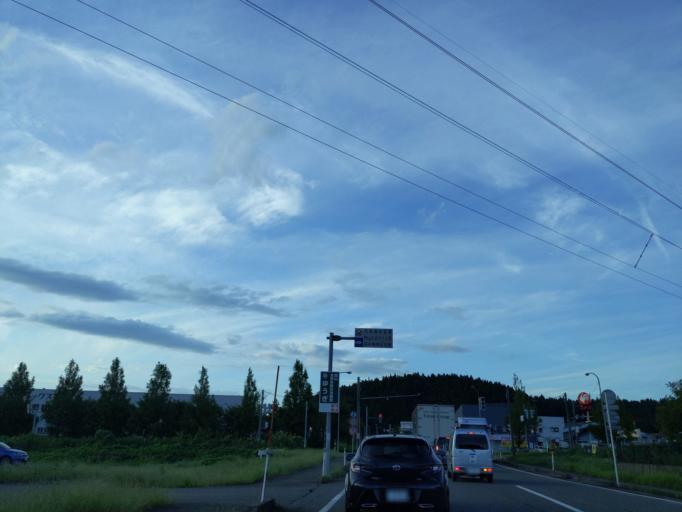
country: JP
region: Niigata
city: Kashiwazaki
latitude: 37.4526
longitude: 138.6555
